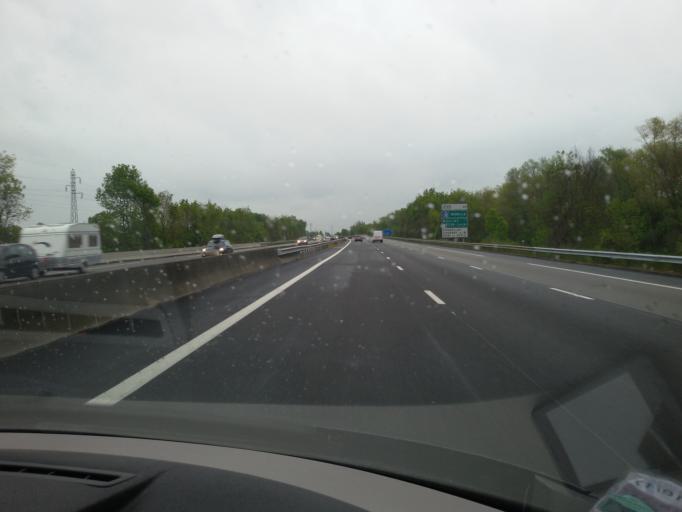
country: FR
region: Rhone-Alpes
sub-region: Departement du Rhone
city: Belleville
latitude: 46.1061
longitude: 4.7564
